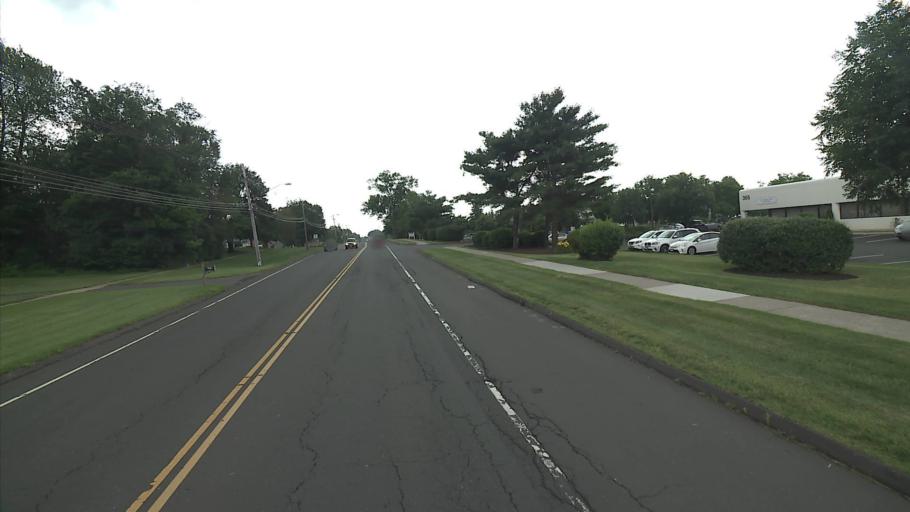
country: US
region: Connecticut
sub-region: Hartford County
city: Newington
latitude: 41.7087
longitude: -72.7362
